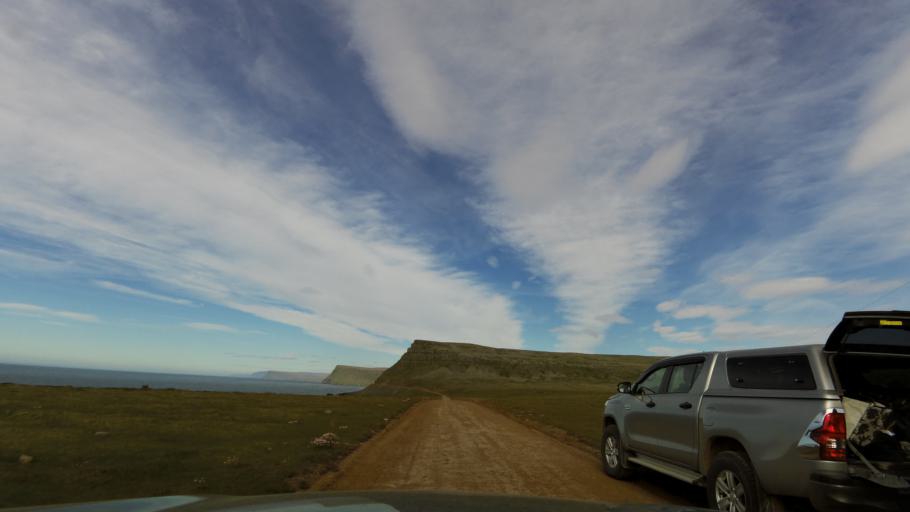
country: IS
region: West
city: Olafsvik
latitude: 65.5030
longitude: -24.5265
